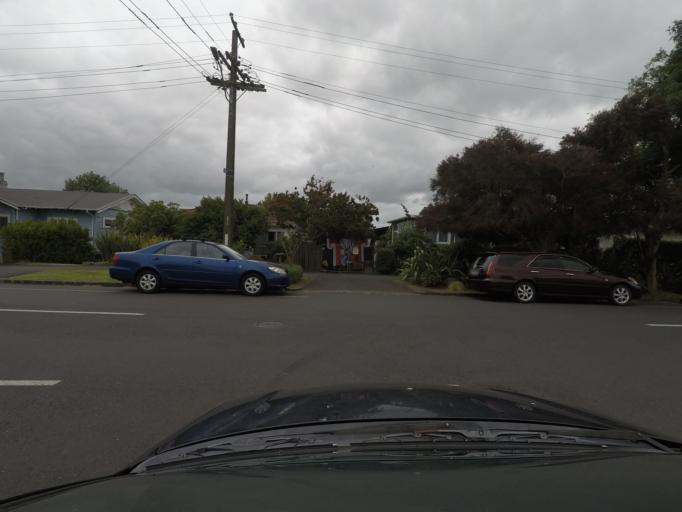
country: NZ
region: Auckland
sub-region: Auckland
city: Rosebank
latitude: -36.8670
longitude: 174.7017
